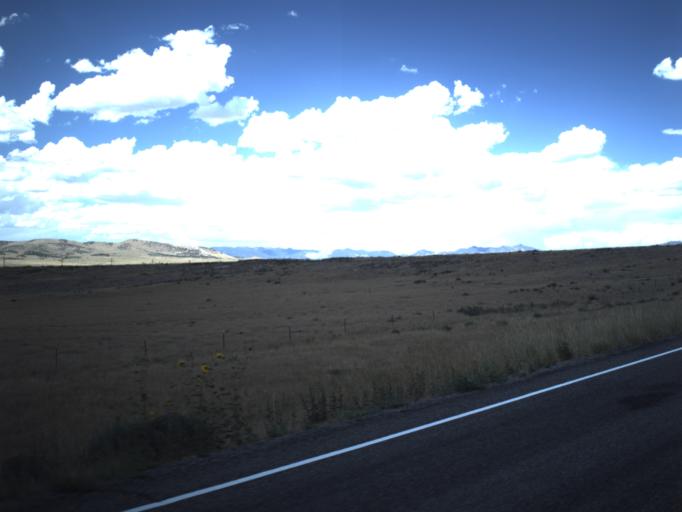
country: US
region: Utah
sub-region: Juab County
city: Nephi
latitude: 39.6813
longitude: -112.2507
